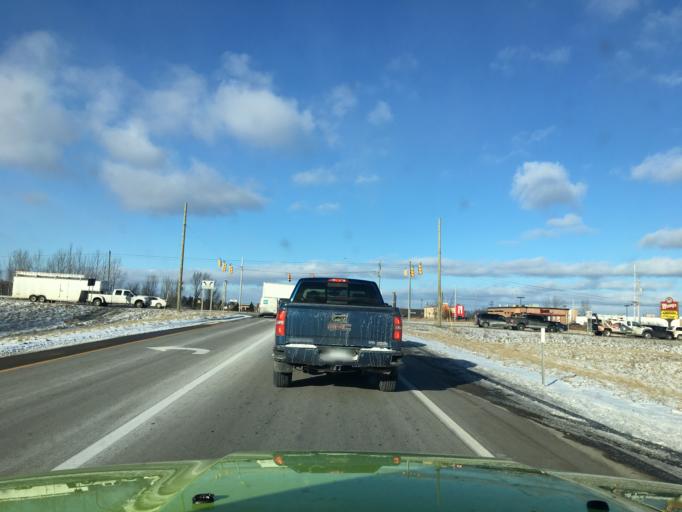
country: US
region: Michigan
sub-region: Kent County
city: Cedar Springs
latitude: 43.2192
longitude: -85.5724
